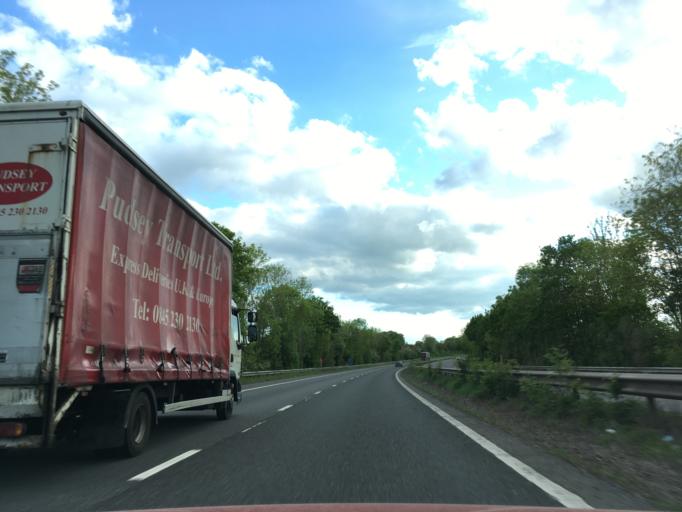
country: GB
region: England
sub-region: Gloucestershire
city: Newent
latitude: 51.9643
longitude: -2.4278
